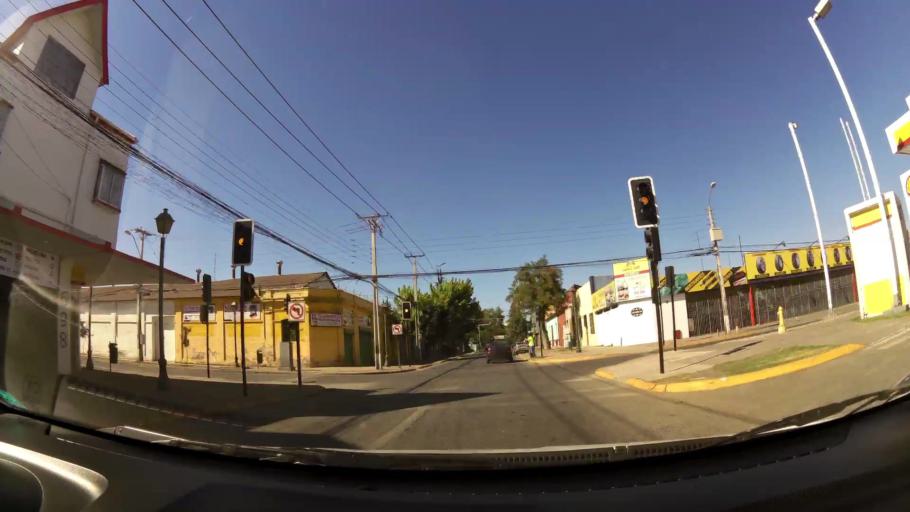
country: CL
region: O'Higgins
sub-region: Provincia de Cachapoal
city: Rancagua
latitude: -34.1723
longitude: -70.7492
